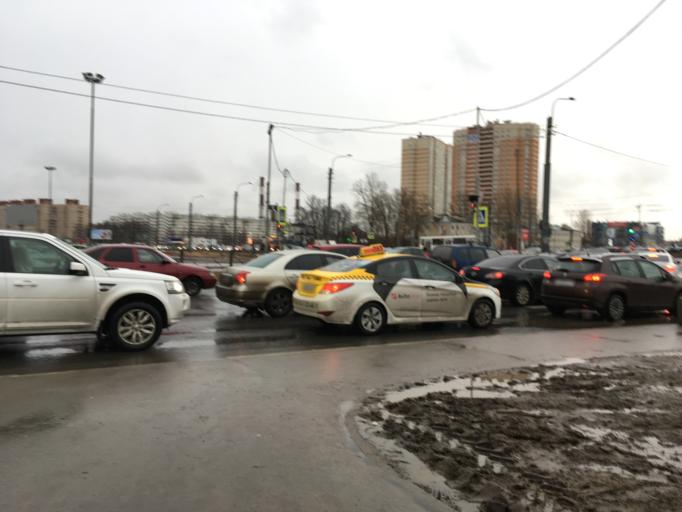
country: RU
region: St.-Petersburg
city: Komendantsky aerodrom
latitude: 59.9999
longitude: 30.2692
